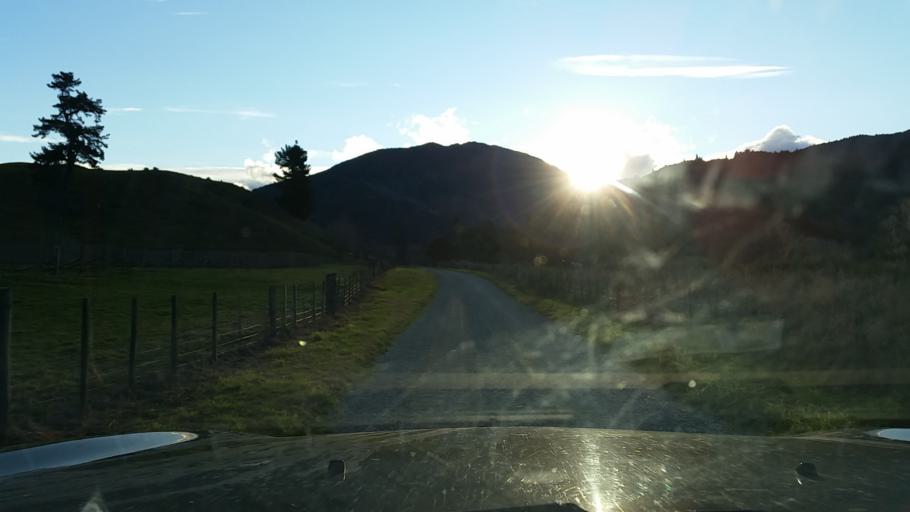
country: NZ
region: Marlborough
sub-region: Marlborough District
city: Blenheim
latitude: -41.5074
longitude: 173.5823
